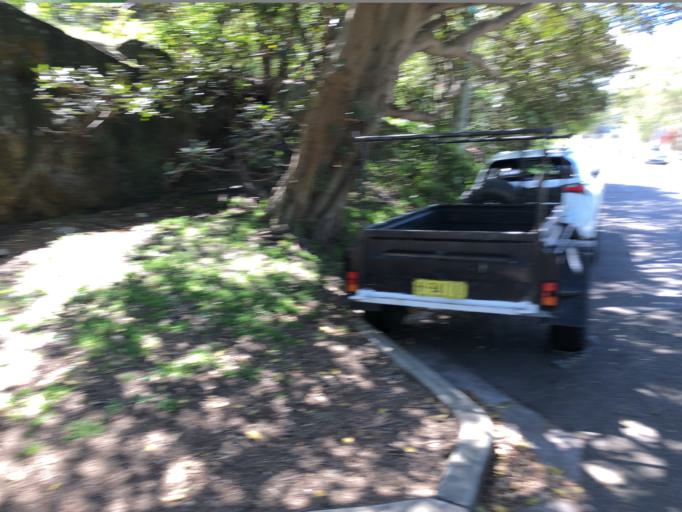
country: AU
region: New South Wales
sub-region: North Sydney
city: Wollstonecraft
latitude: -33.8434
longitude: 151.1951
